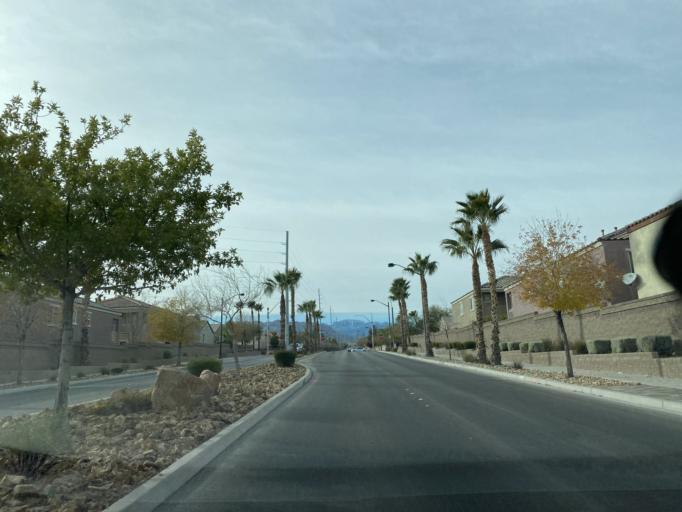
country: US
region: Nevada
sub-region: Clark County
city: Summerlin South
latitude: 36.2992
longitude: -115.2953
